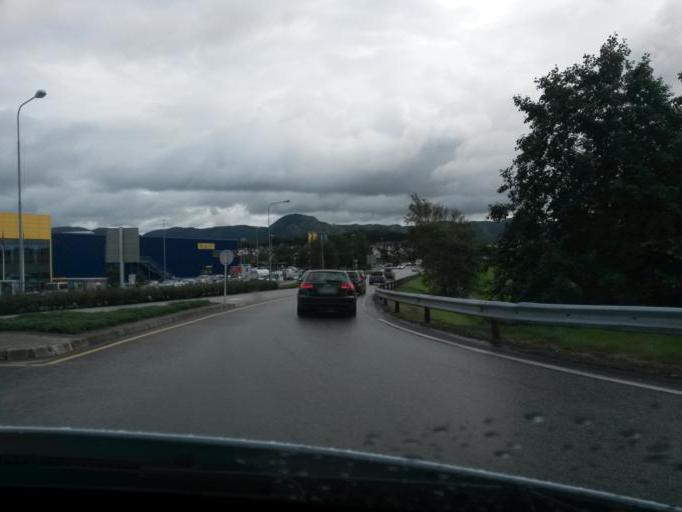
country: NO
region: Rogaland
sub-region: Sandnes
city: Sandnes
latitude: 58.8864
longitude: 5.7198
